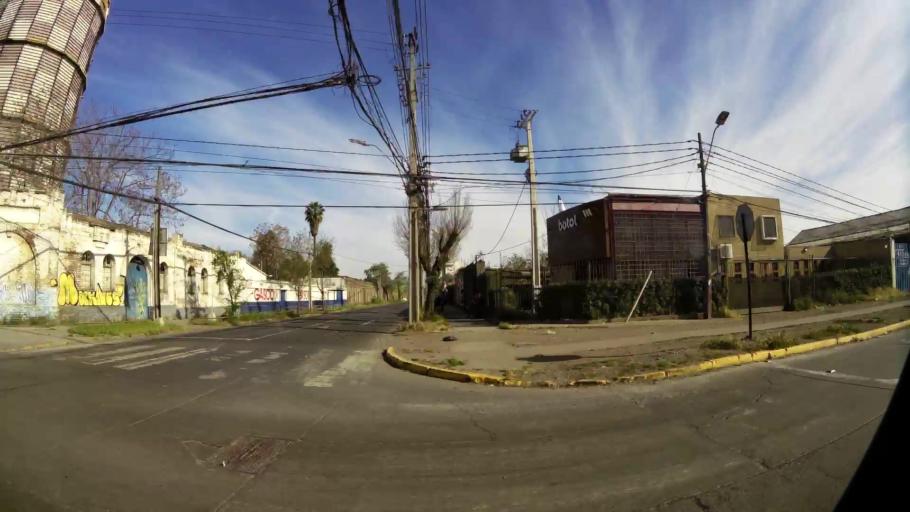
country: CL
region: Santiago Metropolitan
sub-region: Provincia de Santiago
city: Santiago
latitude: -33.4669
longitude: -70.6845
